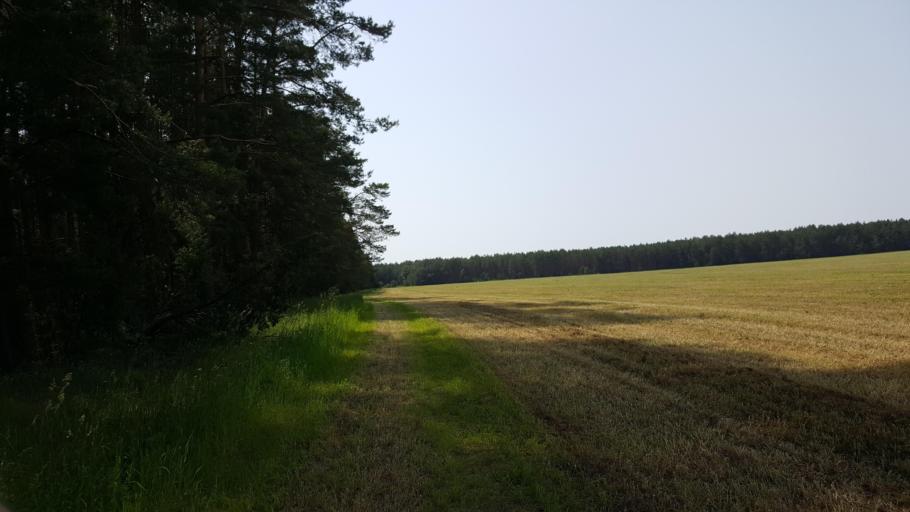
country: BY
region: Brest
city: Kamyanyuki
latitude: 52.5155
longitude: 23.8340
